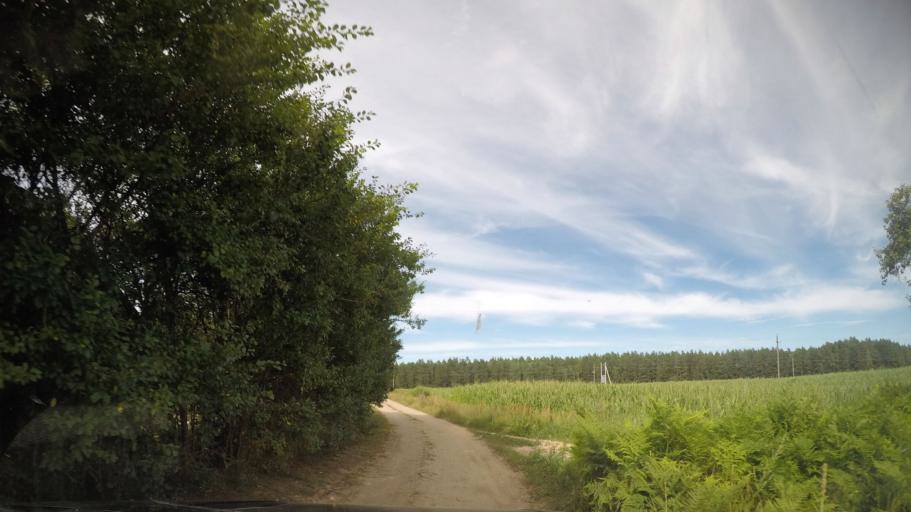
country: BY
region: Grodnenskaya
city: Skidal'
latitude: 53.8376
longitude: 24.1925
